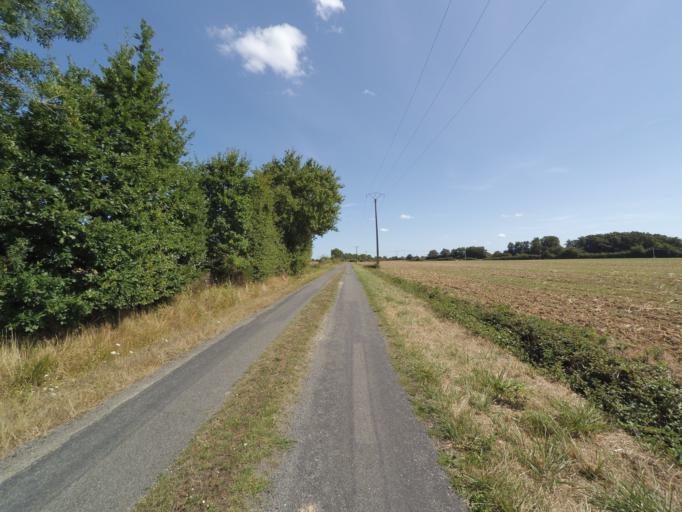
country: FR
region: Pays de la Loire
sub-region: Departement de la Loire-Atlantique
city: Vieillevigne
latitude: 46.9619
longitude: -1.4118
